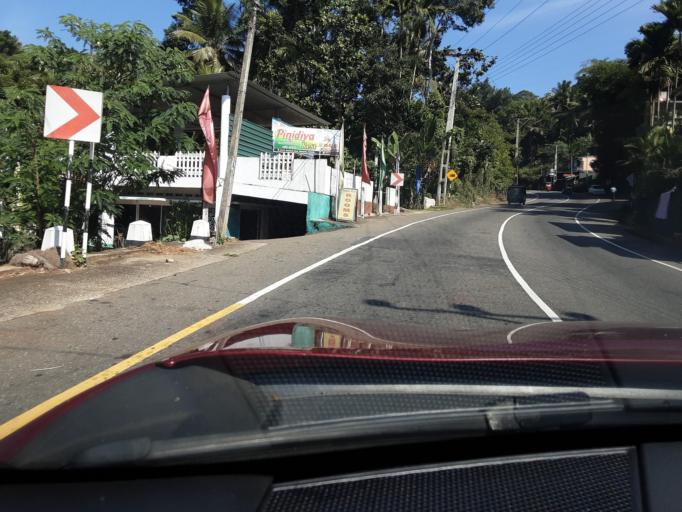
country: LK
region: Uva
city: Badulla
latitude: 7.0097
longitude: 81.0563
